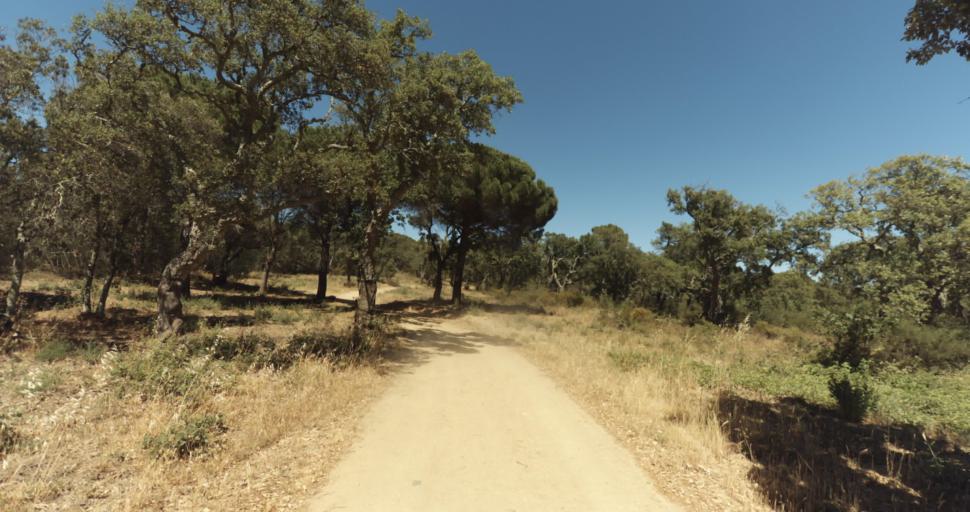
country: FR
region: Provence-Alpes-Cote d'Azur
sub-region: Departement du Var
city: Gassin
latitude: 43.2488
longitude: 6.5623
